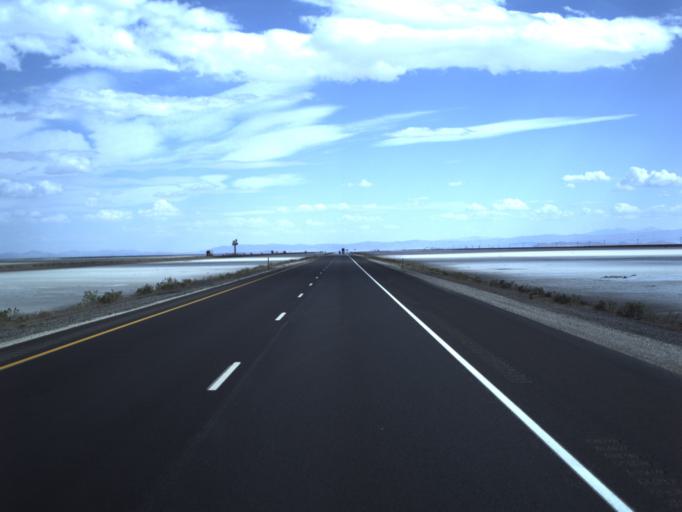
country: US
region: Utah
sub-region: Tooele County
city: Wendover
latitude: 40.7325
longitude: -113.5685
